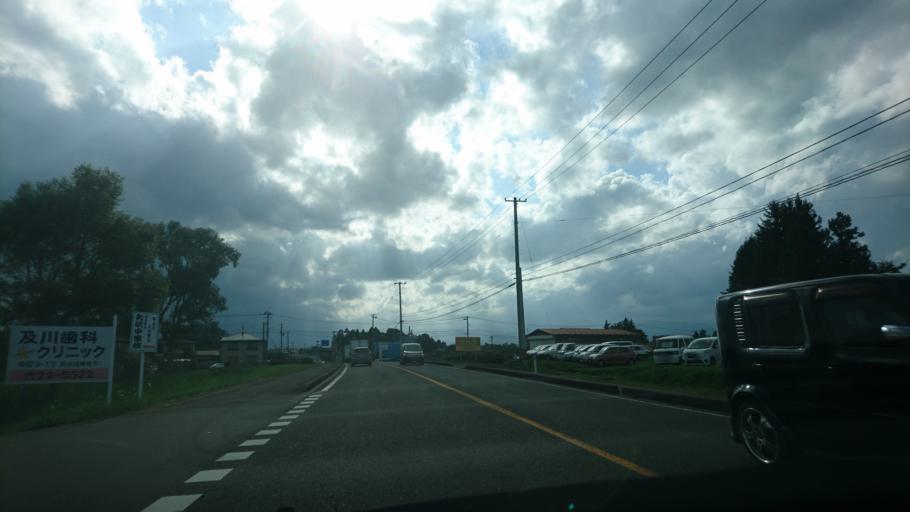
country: JP
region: Iwate
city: Hanamaki
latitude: 39.3923
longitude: 141.1559
